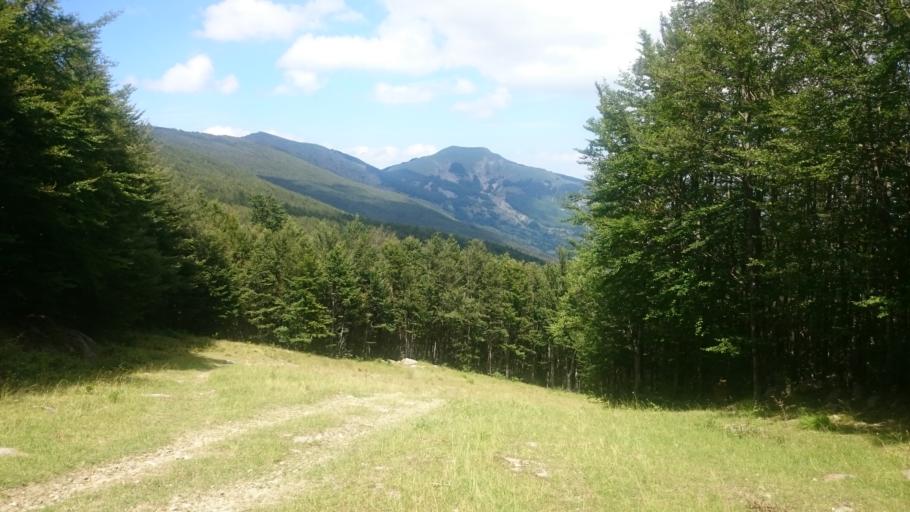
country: IT
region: Emilia-Romagna
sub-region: Provincia di Reggio Emilia
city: Villa Minozzo
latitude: 44.3037
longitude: 10.4322
